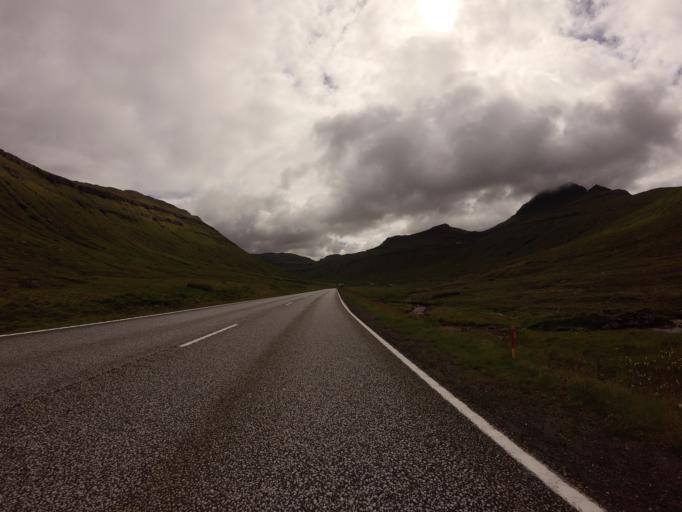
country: FO
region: Streymoy
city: Kollafjordhur
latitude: 62.1155
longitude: -6.9738
